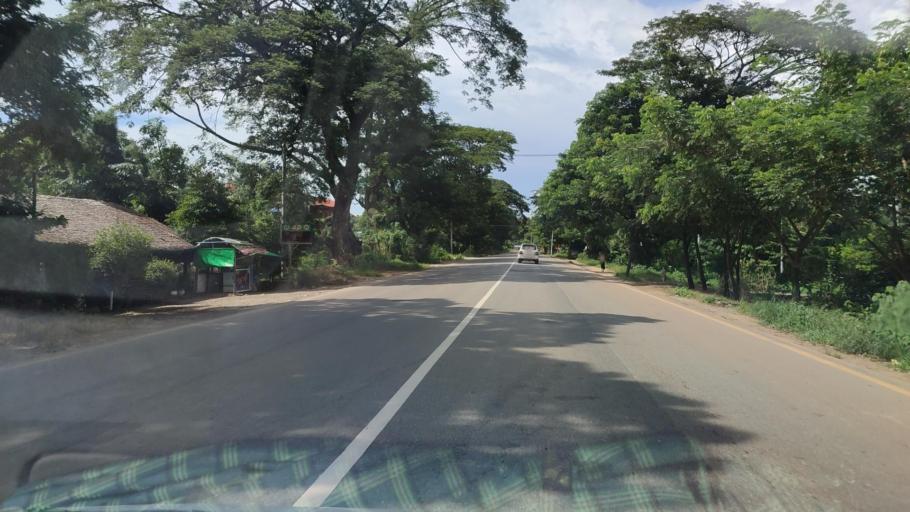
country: MM
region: Bago
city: Pyu
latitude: 18.2176
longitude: 96.5645
